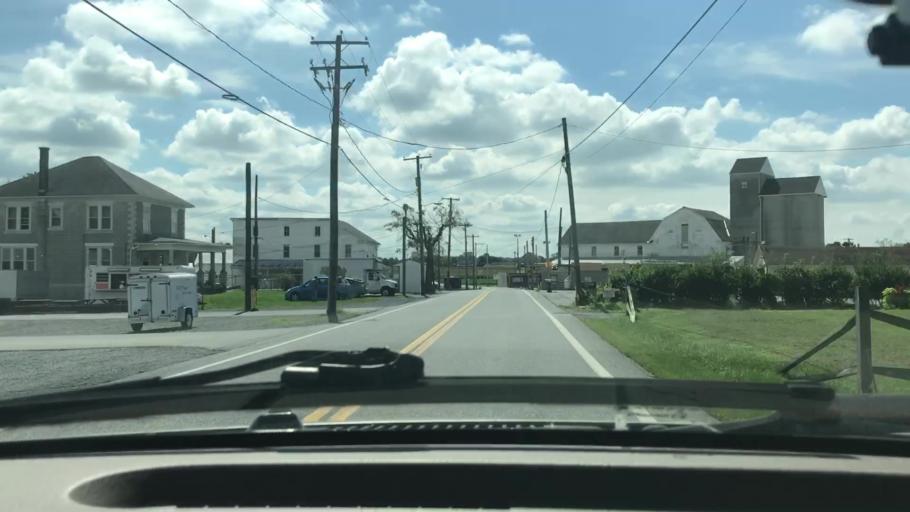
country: US
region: Pennsylvania
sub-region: Lancaster County
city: East Petersburg
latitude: 40.1192
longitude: -76.3795
